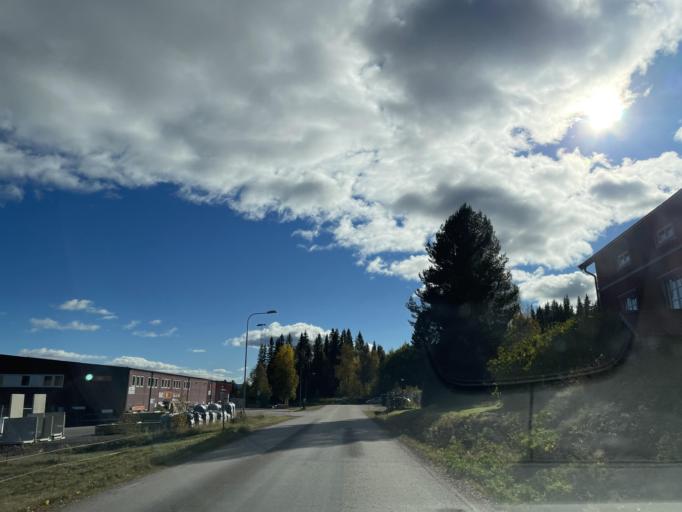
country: SE
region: Dalarna
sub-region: Malung-Saelens kommun
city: Malung
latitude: 61.1316
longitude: 13.2764
